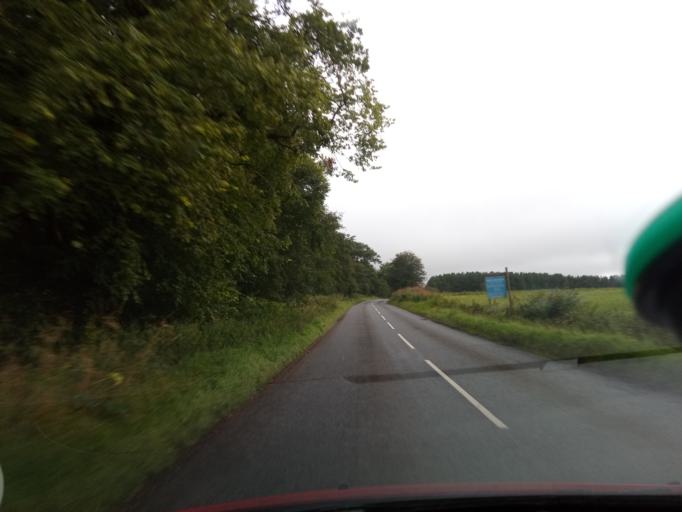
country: GB
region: Scotland
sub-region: The Scottish Borders
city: Saint Boswells
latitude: 55.6540
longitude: -2.5479
